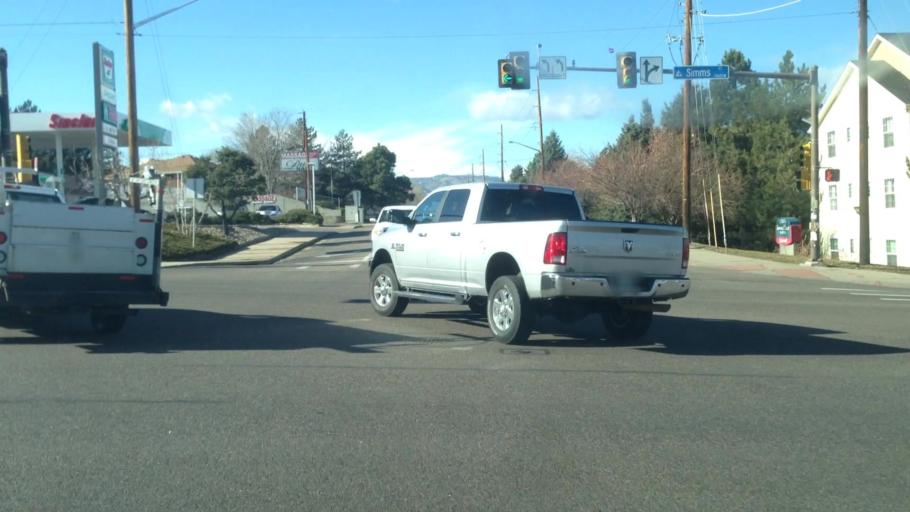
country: US
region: Colorado
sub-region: Jefferson County
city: Applewood
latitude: 39.7291
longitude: -105.1283
